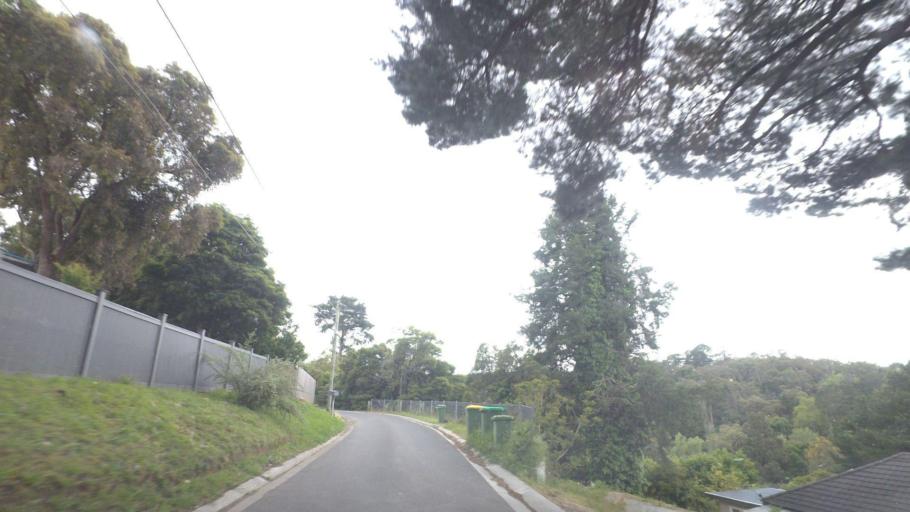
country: AU
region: Victoria
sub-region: Yarra Ranges
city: Mount Evelyn
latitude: -37.7905
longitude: 145.3735
